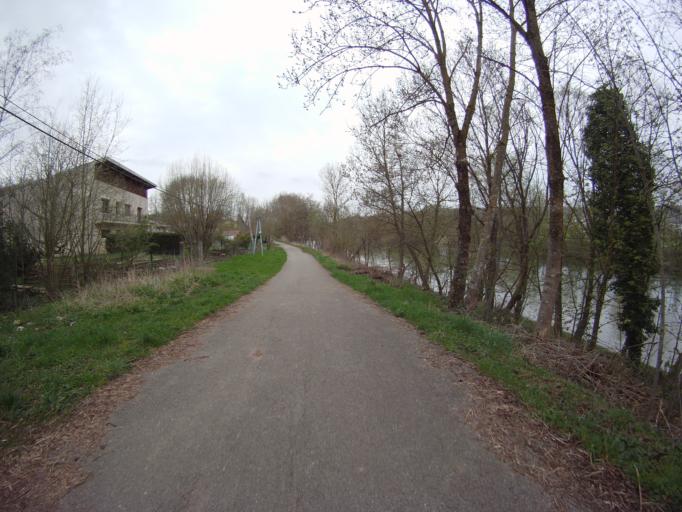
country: FR
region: Lorraine
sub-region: Departement de Meurthe-et-Moselle
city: Pont-Saint-Vincent
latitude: 48.6098
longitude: 6.0902
